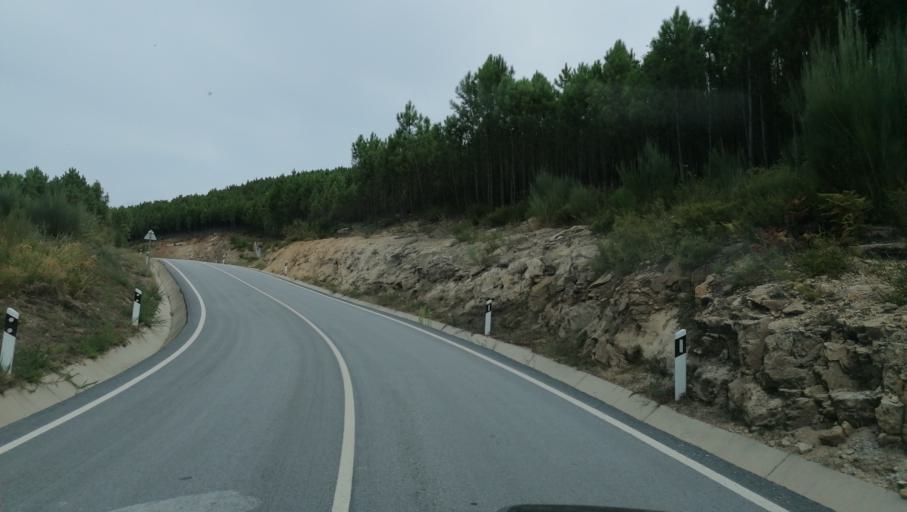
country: PT
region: Vila Real
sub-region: Vila Pouca de Aguiar
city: Vila Pouca de Aguiar
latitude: 41.5553
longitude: -7.7102
